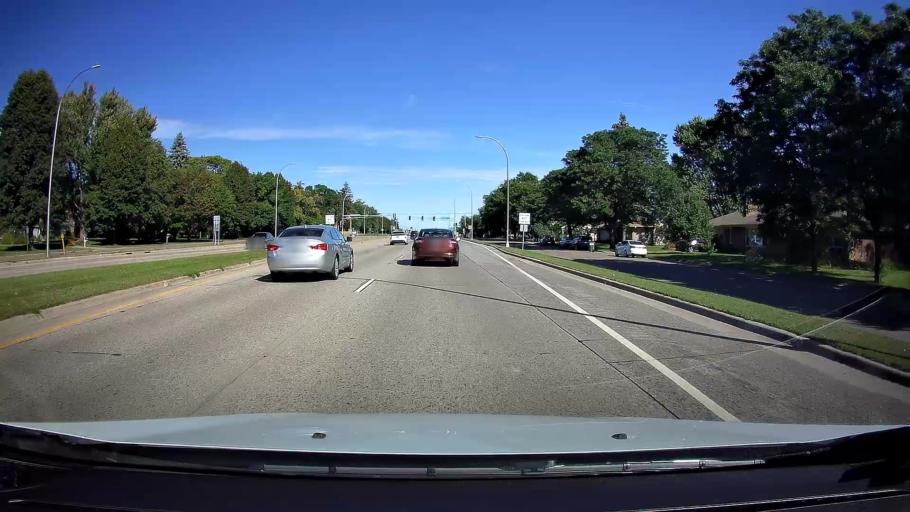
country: US
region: Minnesota
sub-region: Ramsey County
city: Falcon Heights
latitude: 44.9975
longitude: -93.1665
